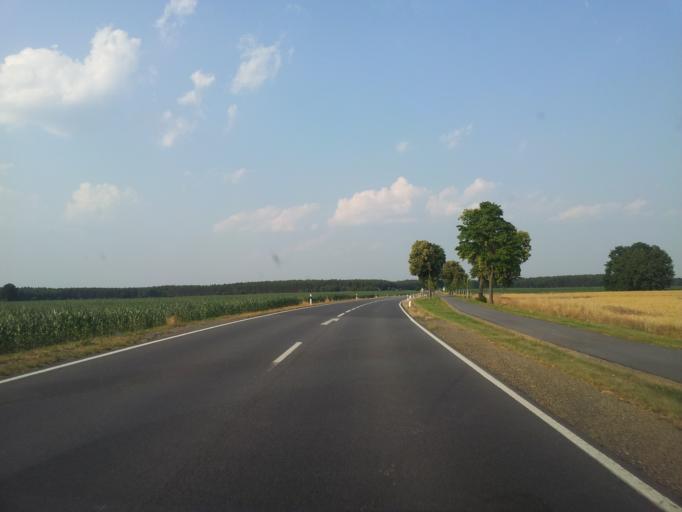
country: DE
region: Saxony
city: Wiednitz
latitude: 51.3501
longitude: 14.0200
